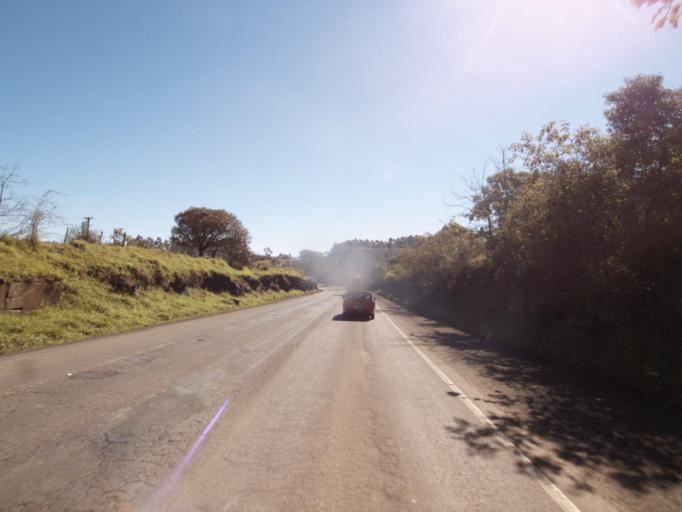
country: AR
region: Misiones
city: Bernardo de Irigoyen
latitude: -26.7700
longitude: -53.4638
